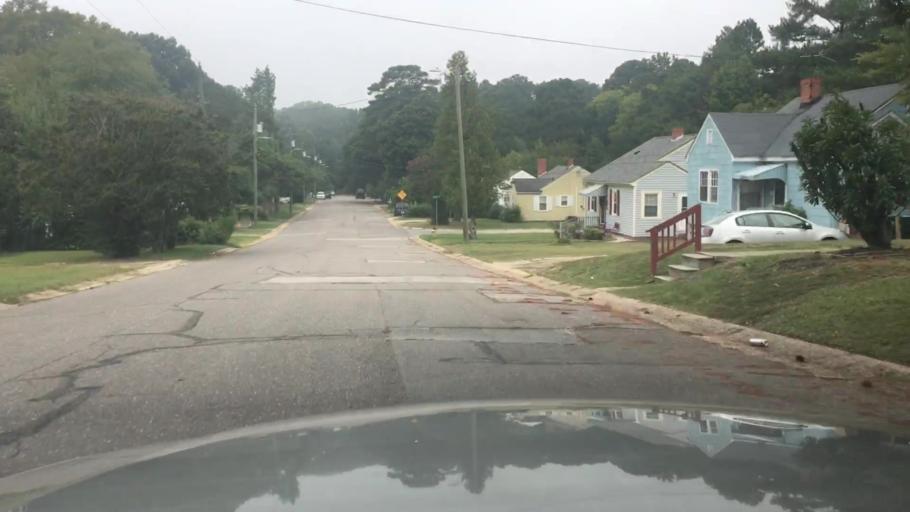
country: US
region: North Carolina
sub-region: Cumberland County
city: Fayetteville
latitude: 35.0744
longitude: -78.8848
